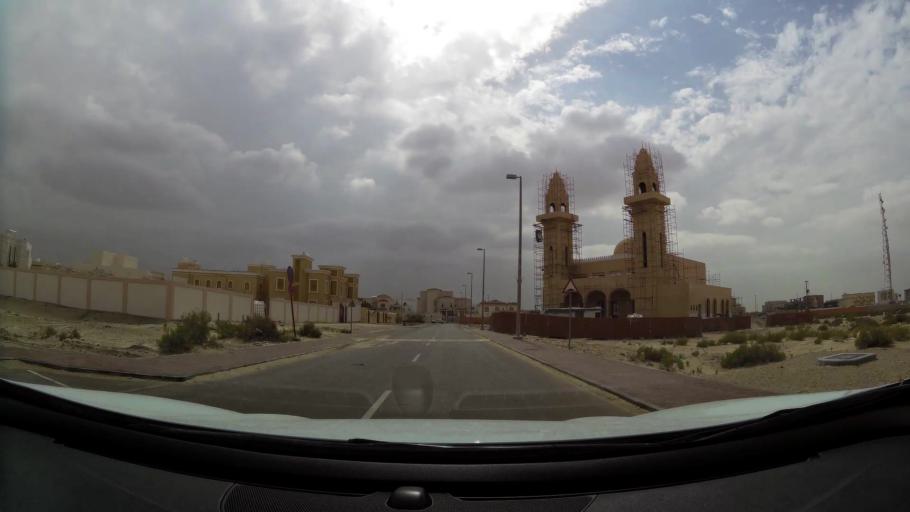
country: AE
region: Abu Dhabi
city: Abu Dhabi
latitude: 24.3837
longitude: 54.6412
